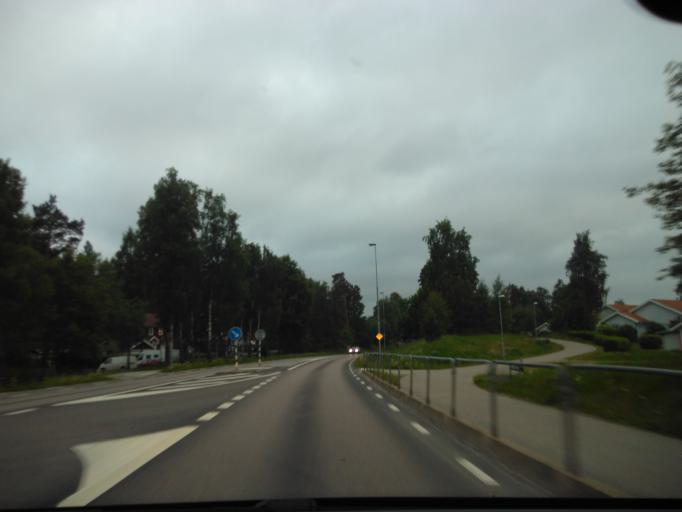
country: SE
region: Vaestra Goetaland
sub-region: Vargarda Kommun
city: Vargarda
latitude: 58.0302
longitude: 12.8034
